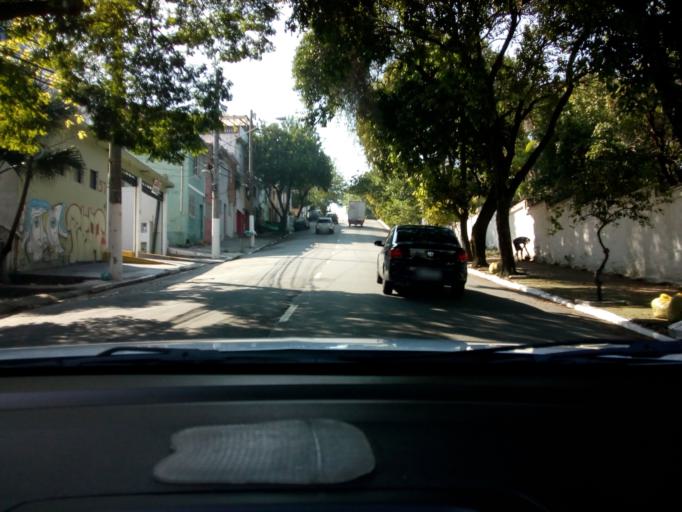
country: BR
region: Sao Paulo
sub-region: Sao Paulo
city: Sao Paulo
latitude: -23.5783
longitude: -46.6278
